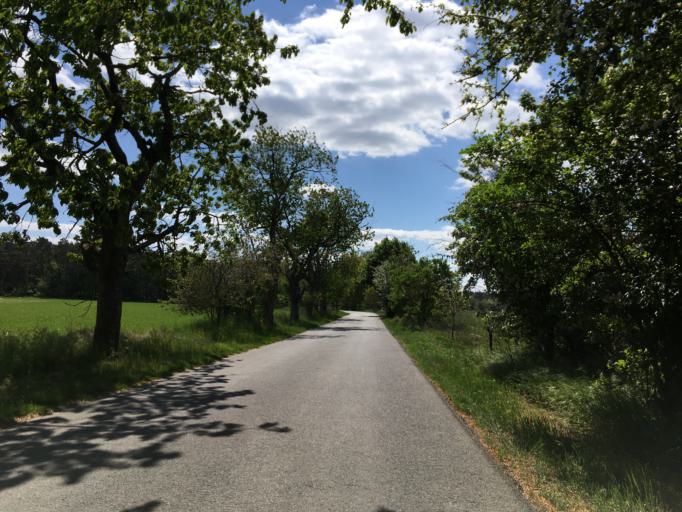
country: DE
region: Brandenburg
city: Rudnitz
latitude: 52.7270
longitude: 13.6607
